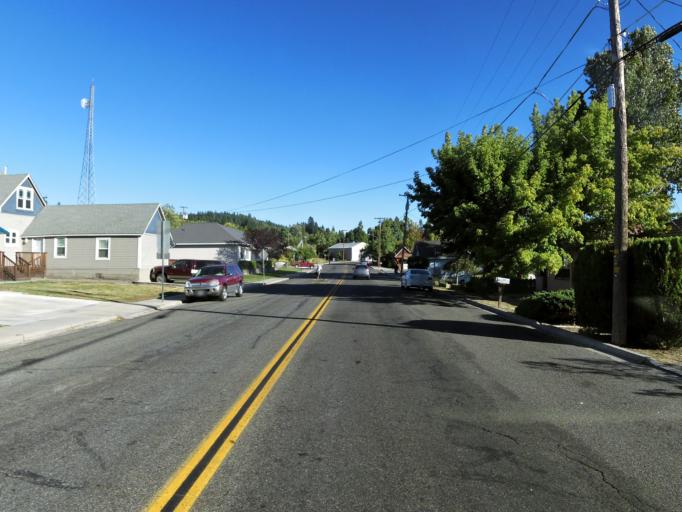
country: US
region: California
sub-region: Siskiyou County
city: Mount Shasta
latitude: 41.3136
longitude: -122.3162
